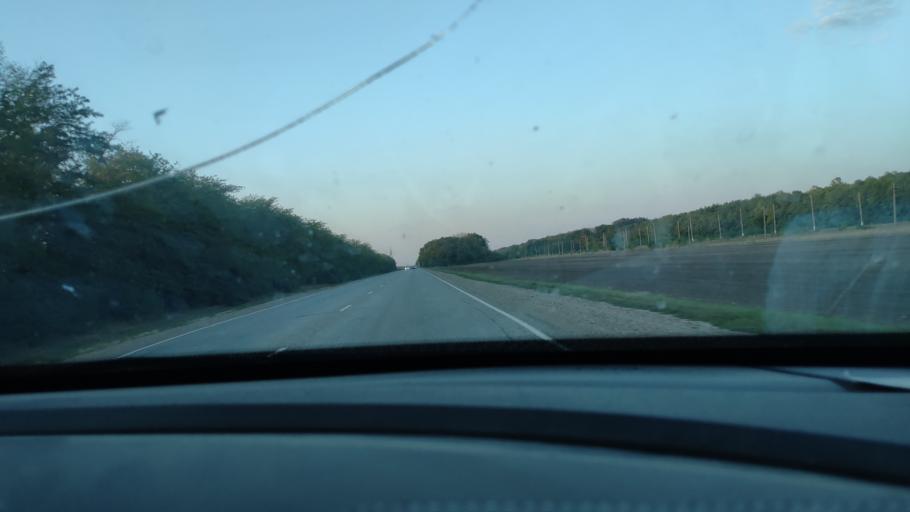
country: RU
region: Krasnodarskiy
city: Starominskaya
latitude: 46.4806
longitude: 39.0514
